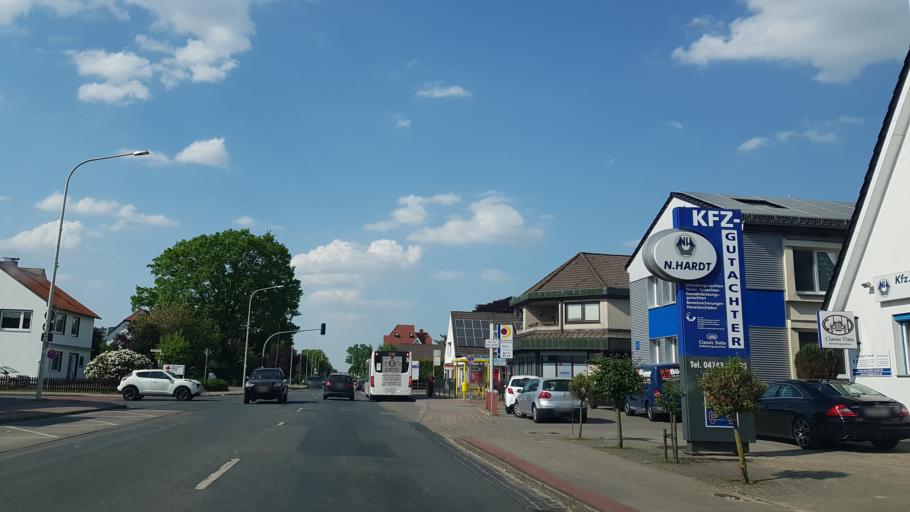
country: DE
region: Lower Saxony
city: Langen
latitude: 53.5973
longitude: 8.5960
